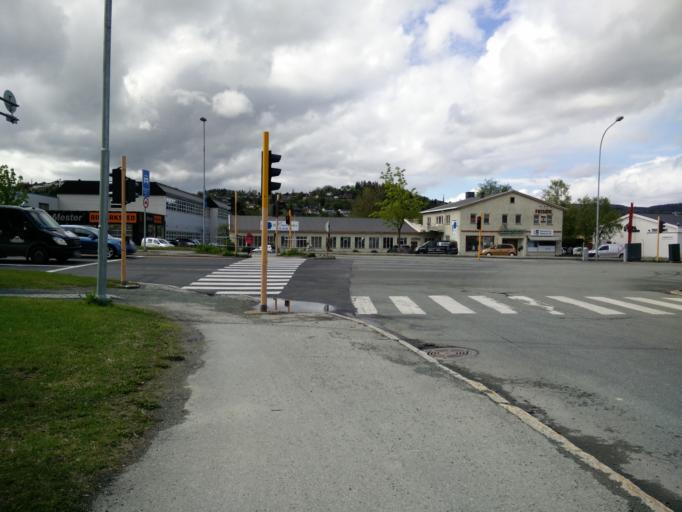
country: NO
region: Sor-Trondelag
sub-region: Trondheim
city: Trondheim
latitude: 63.4043
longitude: 10.3974
